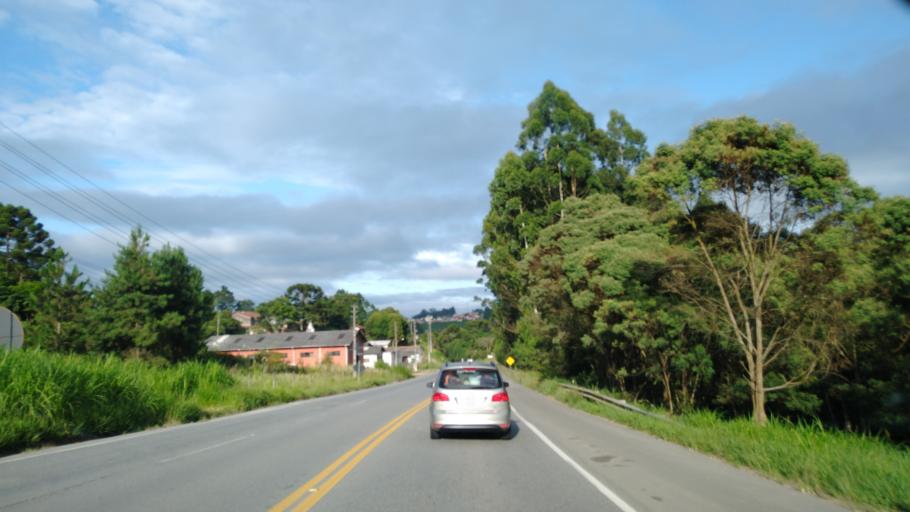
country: BR
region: Santa Catarina
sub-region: Sao Bento Do Sul
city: Sao Bento do Sul
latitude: -26.2377
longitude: -49.4293
